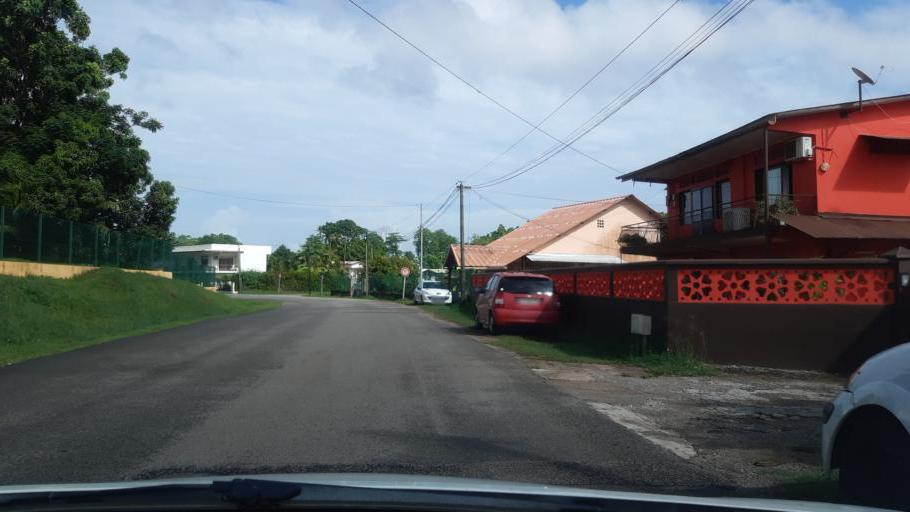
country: GF
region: Guyane
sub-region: Guyane
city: Cayenne
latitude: 4.9420
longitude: -52.3175
